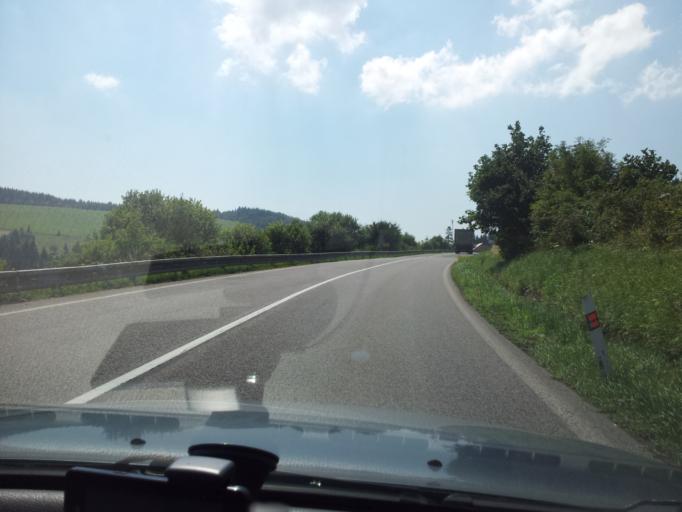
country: SK
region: Zilinsky
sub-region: Okres Dolny Kubin
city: Dolny Kubin
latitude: 49.3076
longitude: 19.3528
